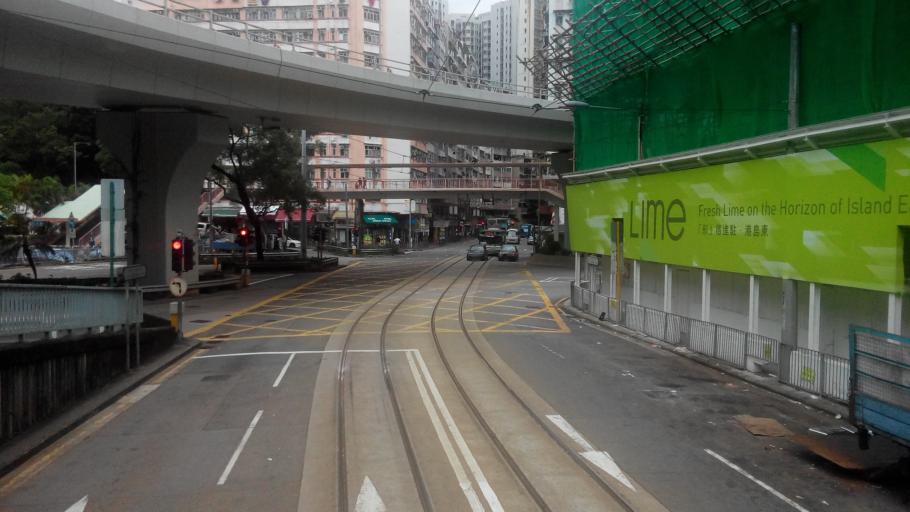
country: HK
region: Wanchai
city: Wan Chai
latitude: 22.2768
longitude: 114.2288
